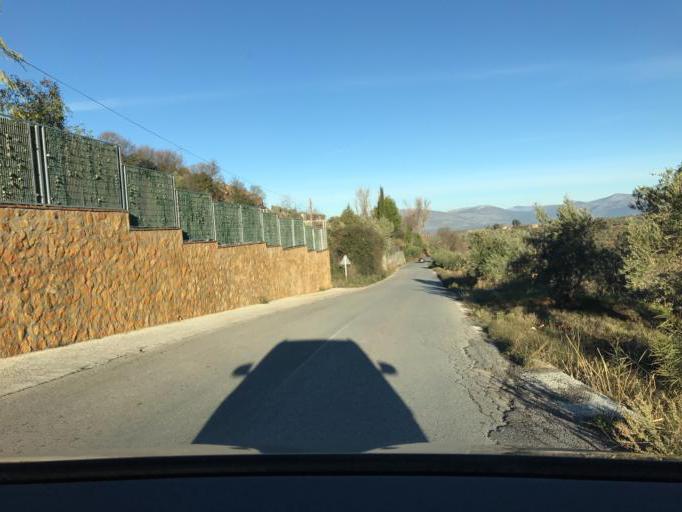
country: ES
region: Andalusia
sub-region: Provincia de Granada
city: Nivar
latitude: 37.2636
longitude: -3.5790
